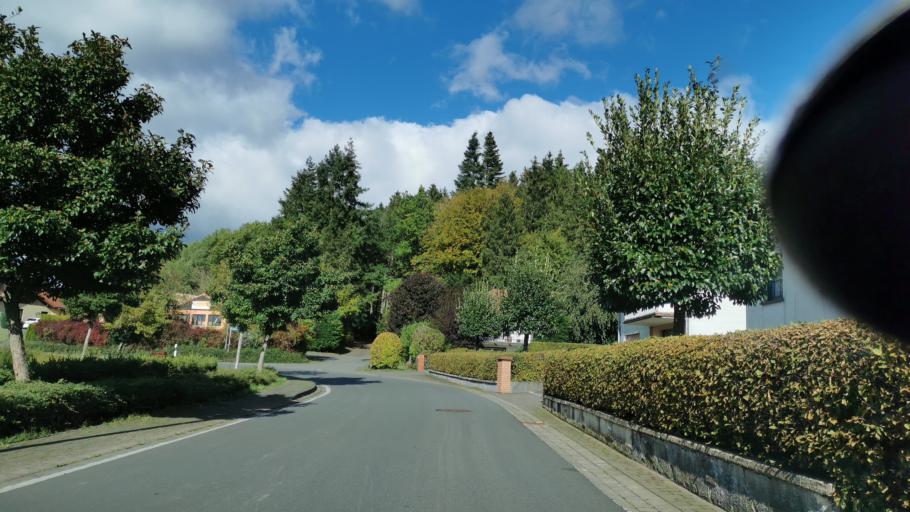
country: DE
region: Rheinland-Pfalz
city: Betteldorf
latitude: 50.2538
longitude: 6.7553
